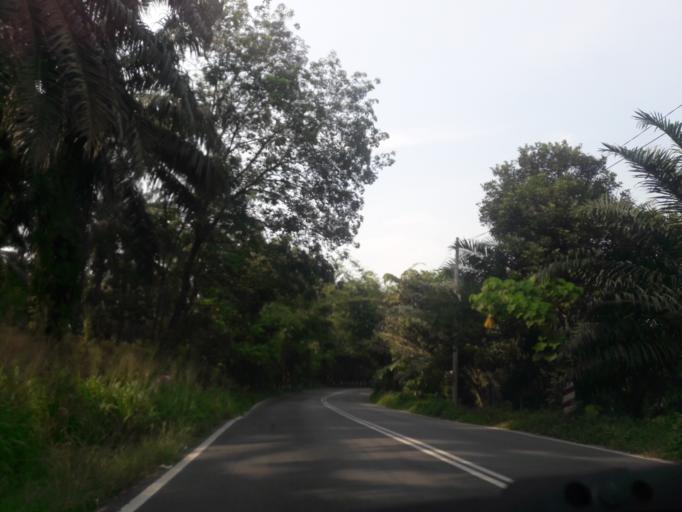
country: MY
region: Kedah
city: Kulim
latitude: 5.3652
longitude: 100.5227
